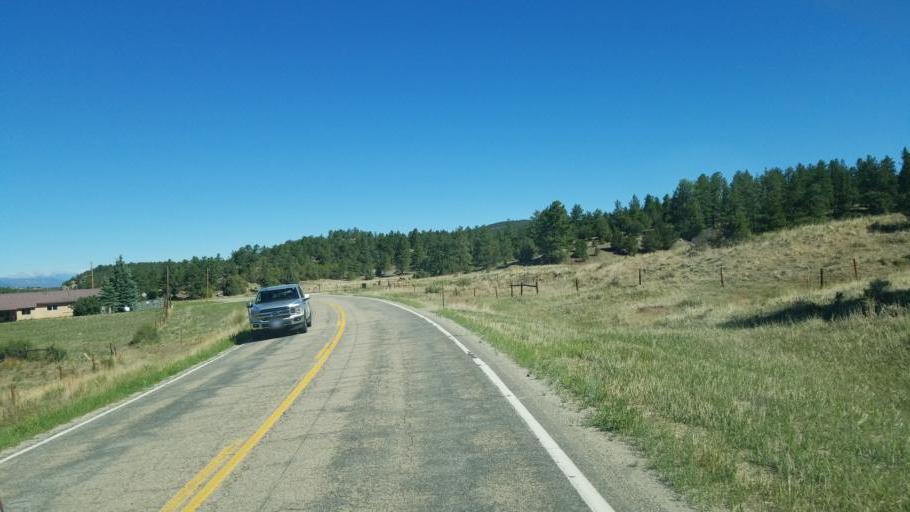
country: US
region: Colorado
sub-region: Custer County
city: Westcliffe
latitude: 38.2336
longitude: -105.5556
